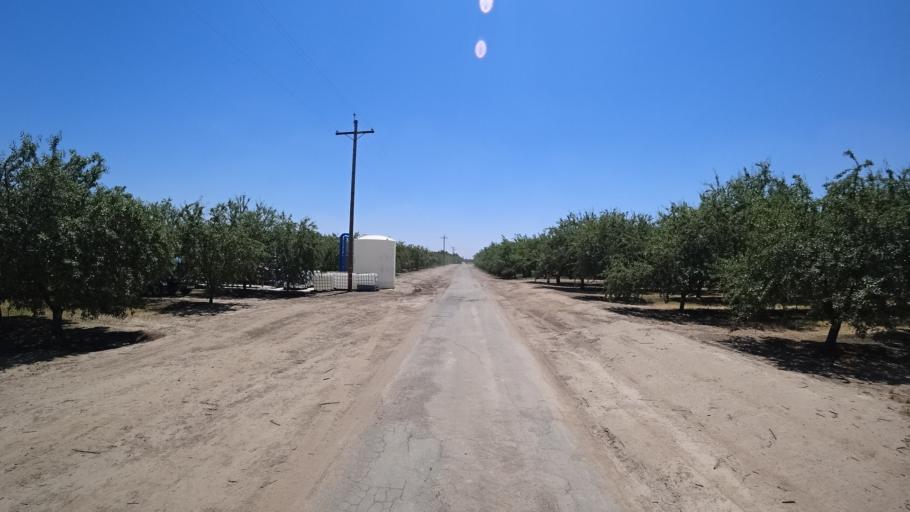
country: US
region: California
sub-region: Kings County
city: Lucerne
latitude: 36.4179
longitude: -119.6279
